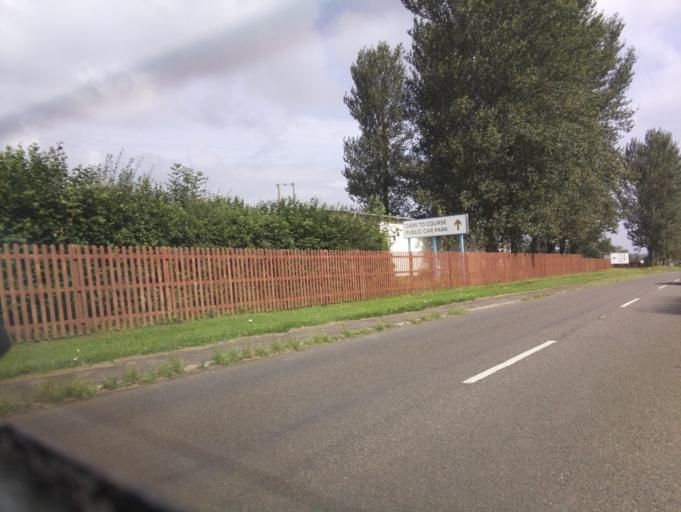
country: GB
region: England
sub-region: Somerset
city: Wincanton
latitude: 51.0664
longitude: -2.4129
